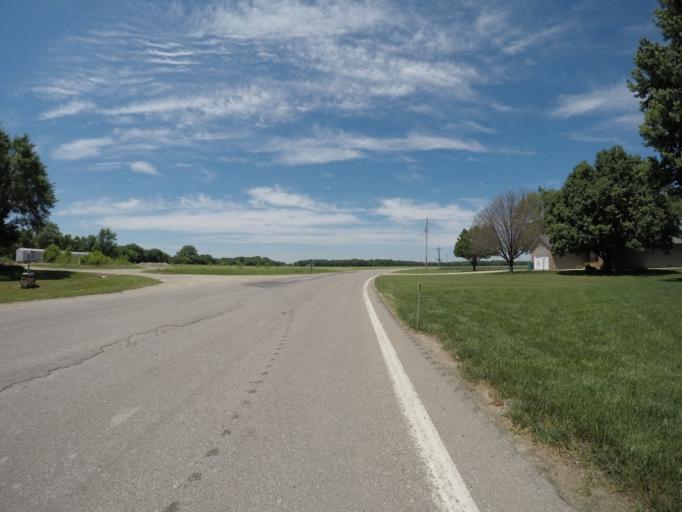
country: US
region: Kansas
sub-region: Wabaunsee County
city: Alma
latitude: 39.0507
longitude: -96.2416
